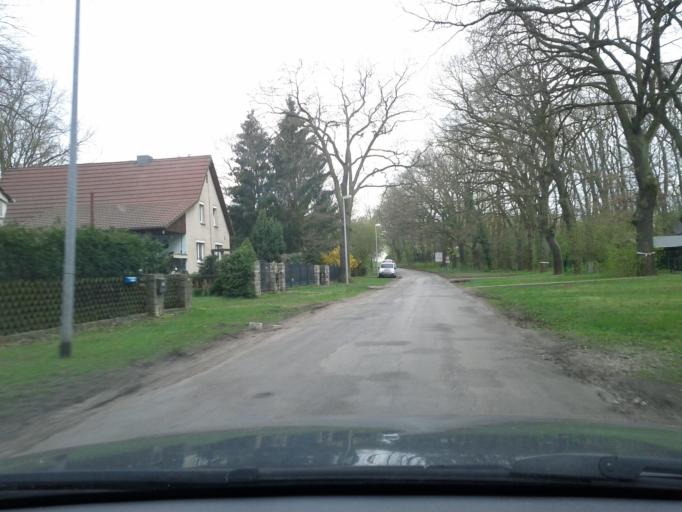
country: DE
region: Brandenburg
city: Schoneiche
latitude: 52.4816
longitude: 13.6891
